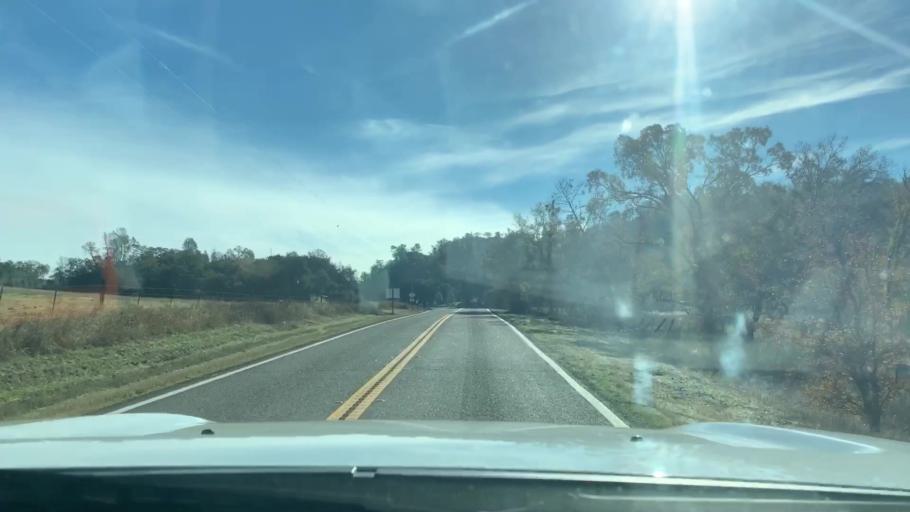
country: US
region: California
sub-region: Fresno County
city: Coalinga
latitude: 36.1696
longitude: -120.6679
